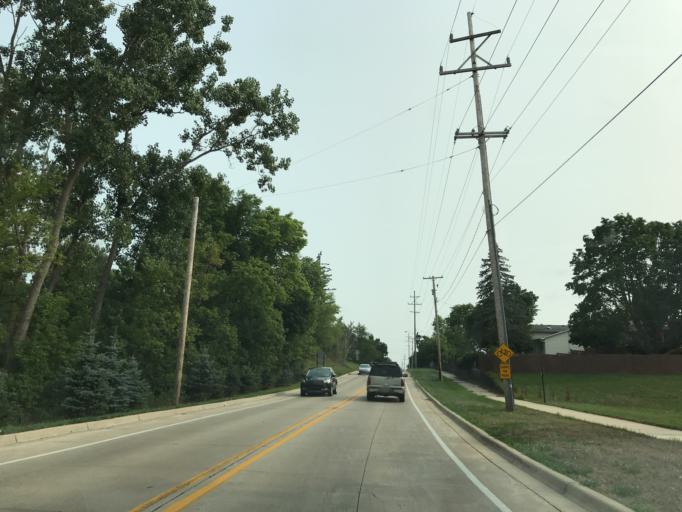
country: US
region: Michigan
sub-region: Ingham County
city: Okemos
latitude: 42.7404
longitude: -84.4475
